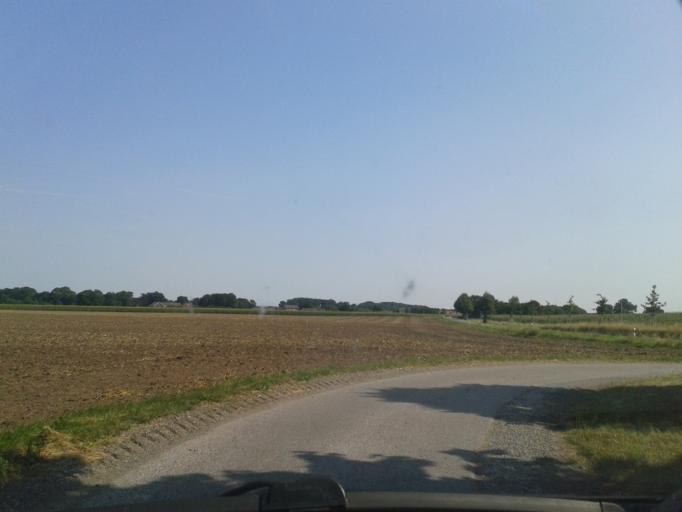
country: DE
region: North Rhine-Westphalia
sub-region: Regierungsbezirk Detmold
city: Hovelhof
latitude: 51.8153
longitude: 8.6032
